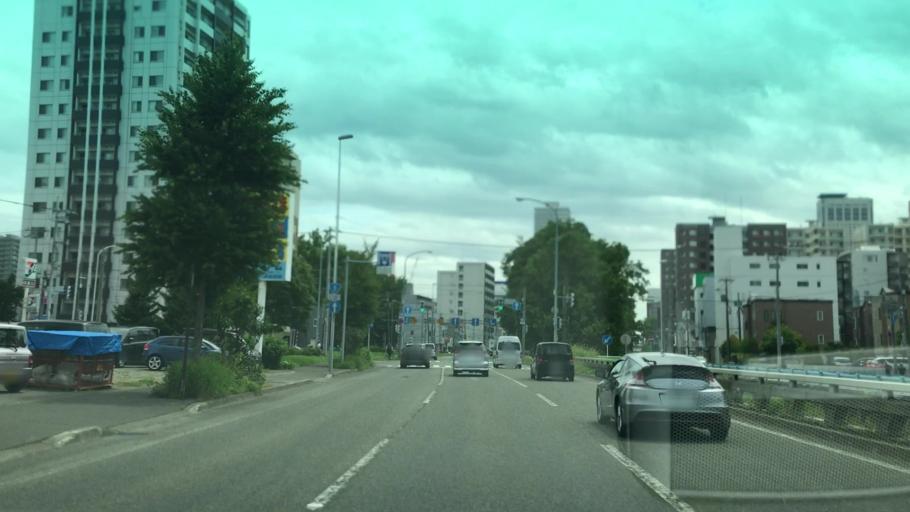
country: JP
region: Hokkaido
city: Sapporo
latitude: 43.0772
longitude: 141.3527
